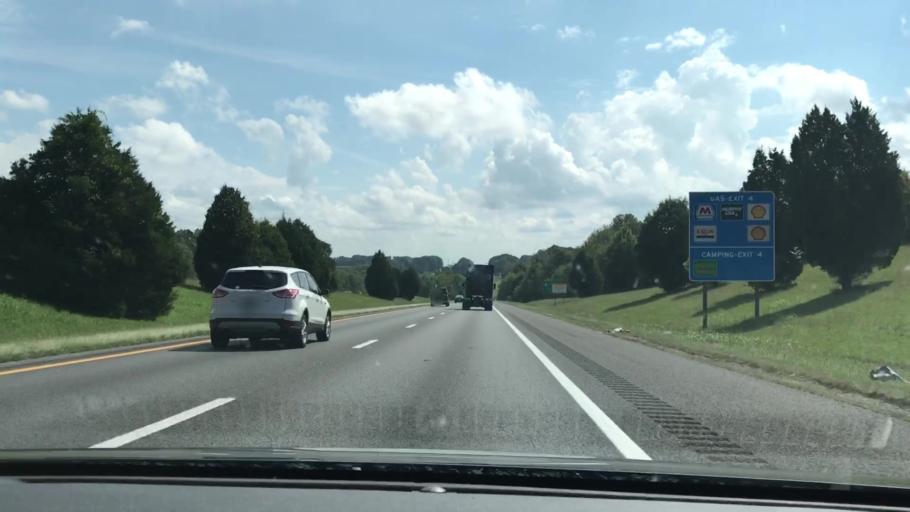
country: US
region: Tennessee
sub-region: Montgomery County
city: Clarksville
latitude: 36.6174
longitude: -87.2984
